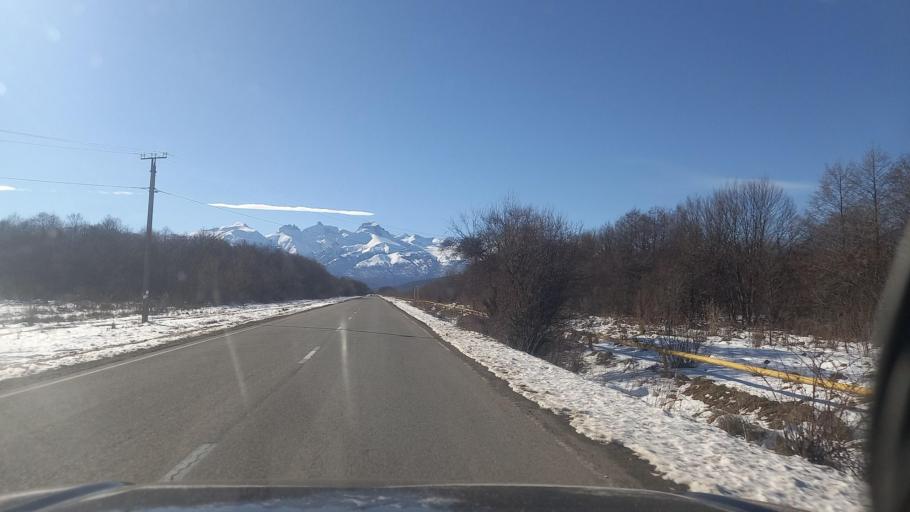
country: RU
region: North Ossetia
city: Chikola
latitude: 43.1628
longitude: 43.8540
